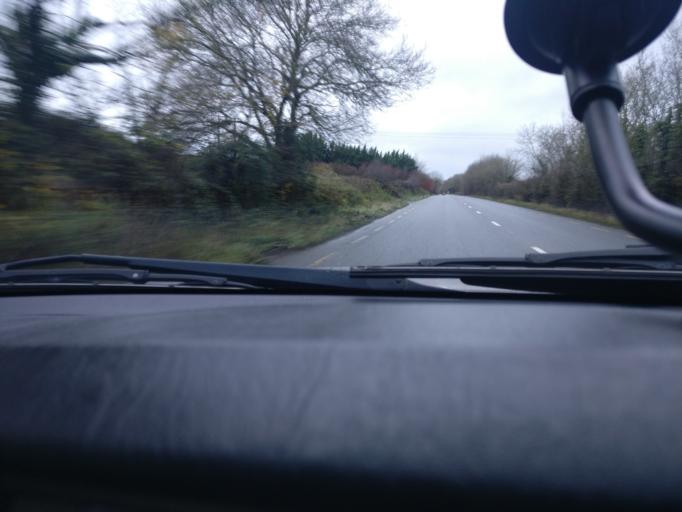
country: IE
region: Leinster
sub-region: Kildare
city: Kilcock
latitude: 53.4153
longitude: -6.7217
